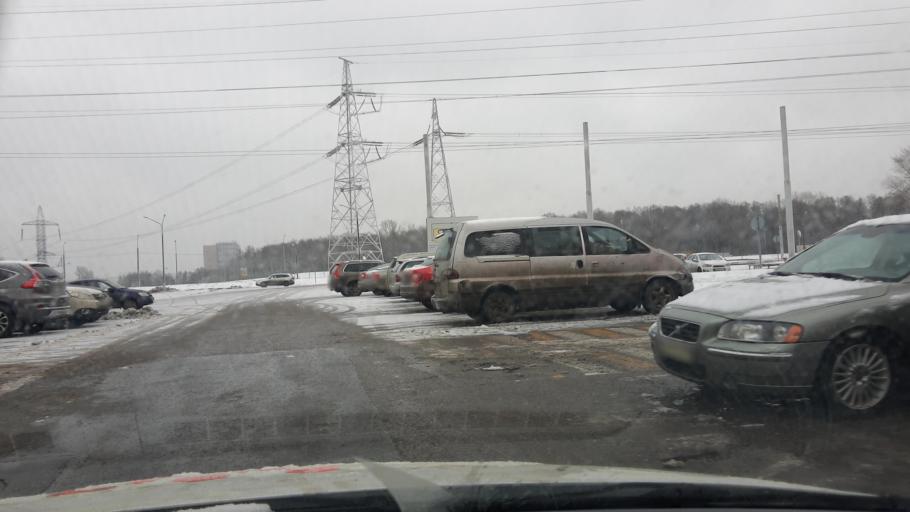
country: RU
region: Moskovskaya
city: Vostryakovo
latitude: 55.6586
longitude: 37.4325
